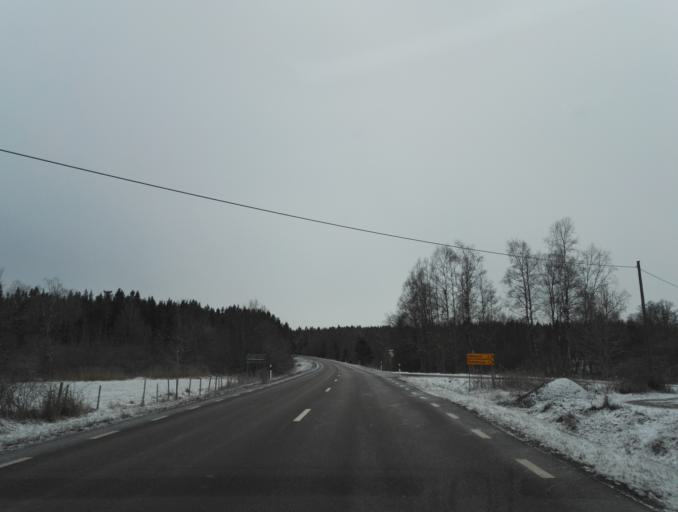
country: SE
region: Kronoberg
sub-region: Uppvidinge Kommun
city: Aseda
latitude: 57.1798
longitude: 15.4976
